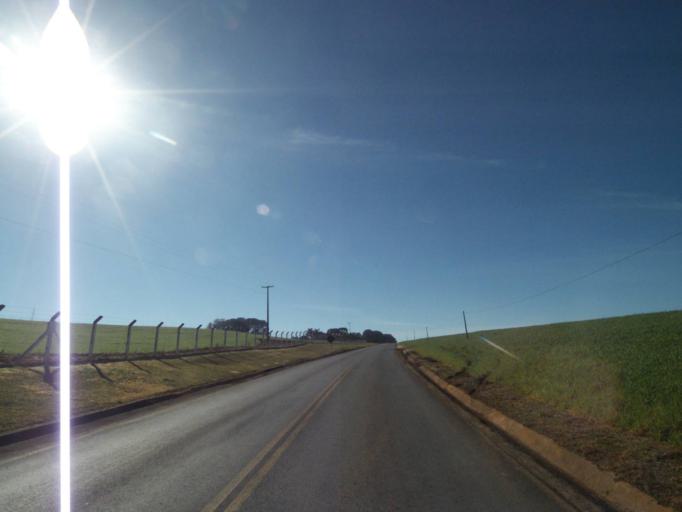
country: BR
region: Parana
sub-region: Tibagi
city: Tibagi
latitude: -24.5256
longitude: -50.3811
